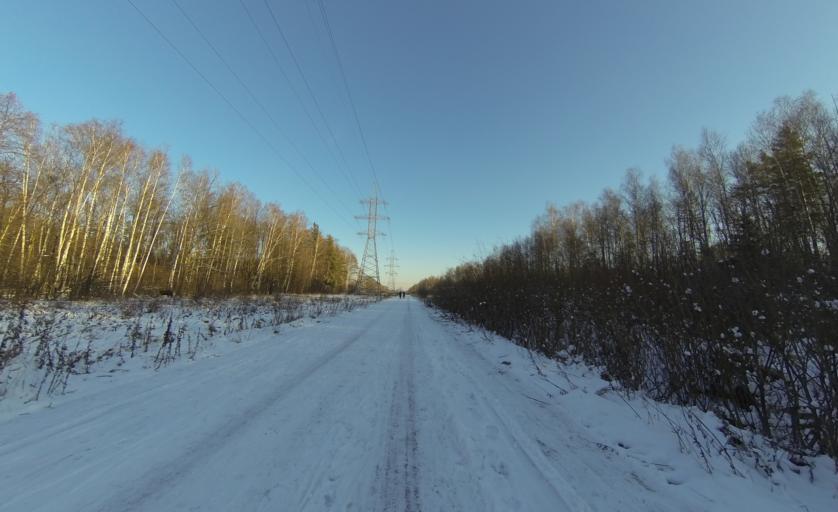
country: RU
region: Moscow
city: Babushkin
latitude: 55.8426
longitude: 37.7407
